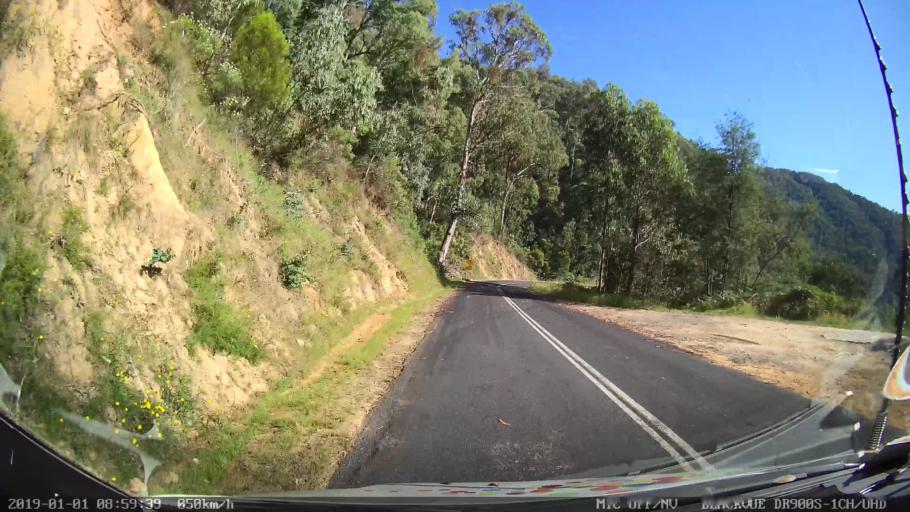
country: AU
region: New South Wales
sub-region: Snowy River
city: Jindabyne
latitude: -36.2397
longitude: 148.1791
